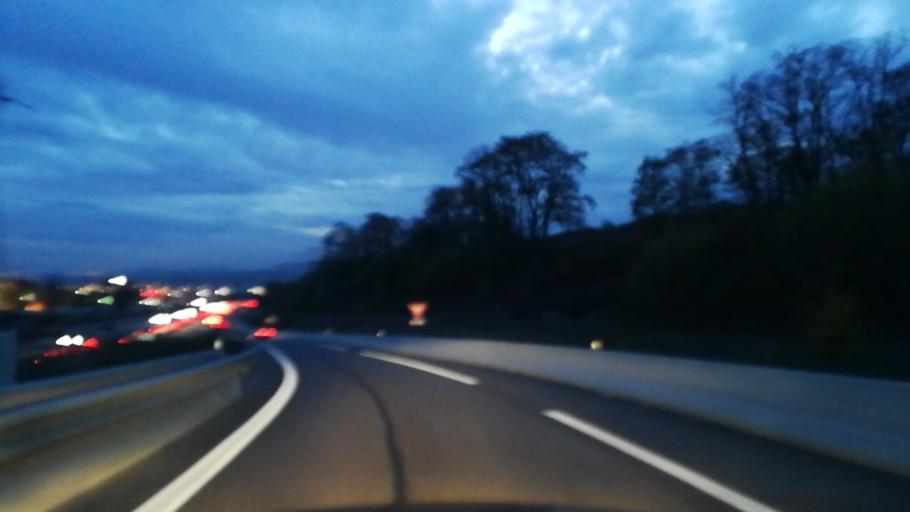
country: FR
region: Bourgogne
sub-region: Departement de la Cote-d'Or
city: Ahuy
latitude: 47.3597
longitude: 5.0454
